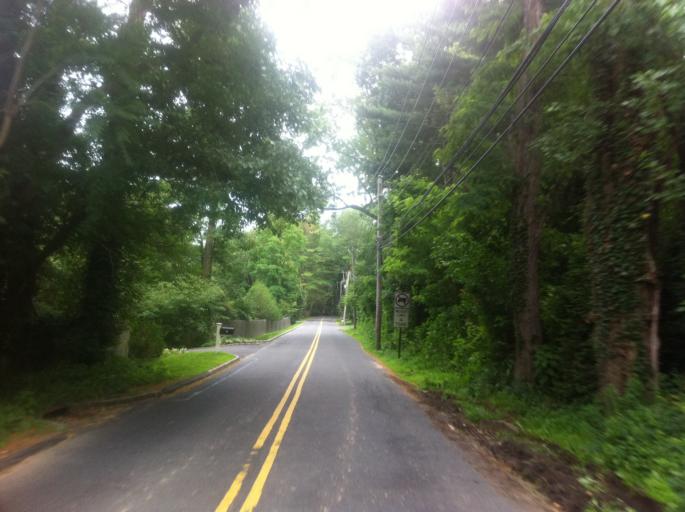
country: US
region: New York
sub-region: Nassau County
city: Bayville
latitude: 40.8941
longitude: -73.5742
